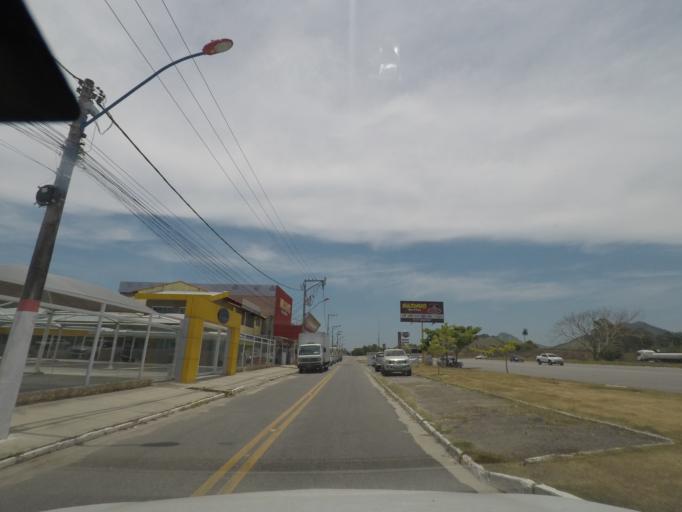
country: BR
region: Rio de Janeiro
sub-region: Marica
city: Marica
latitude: -22.9135
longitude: -42.8449
